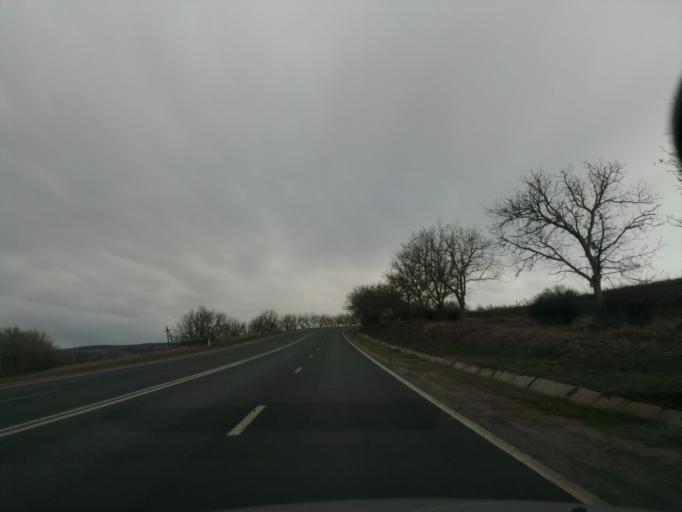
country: MD
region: Laloveni
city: Ialoveni
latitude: 46.9272
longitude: 28.6977
